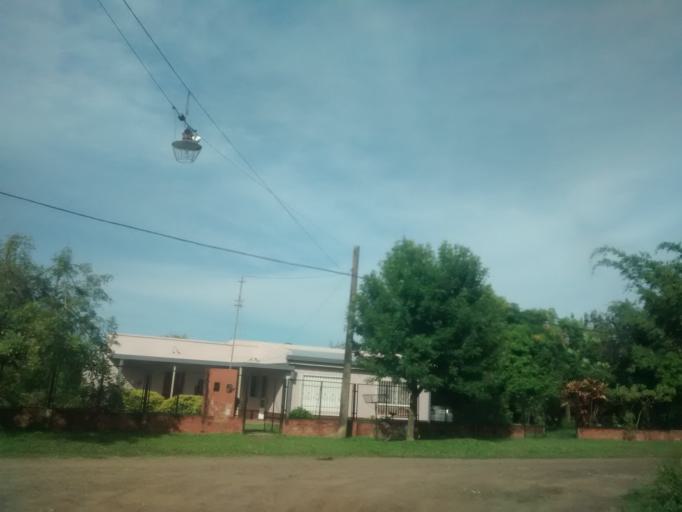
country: AR
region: Chaco
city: Puerto Tirol
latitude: -27.3775
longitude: -59.0974
